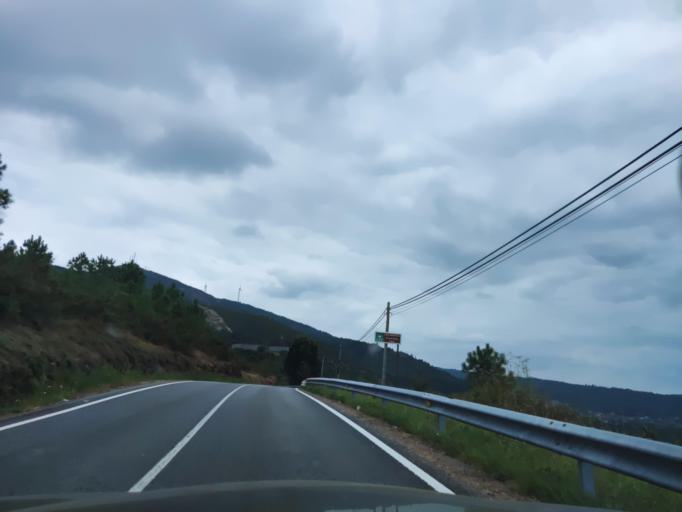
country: ES
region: Galicia
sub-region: Provincia da Coruna
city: Padron
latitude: 42.7383
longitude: -8.6264
